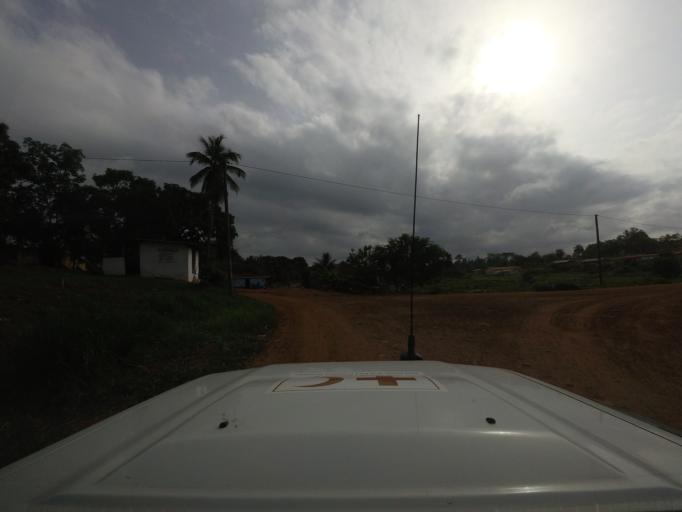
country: LR
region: Bong
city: Gbarnga
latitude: 7.0024
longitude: -9.4747
